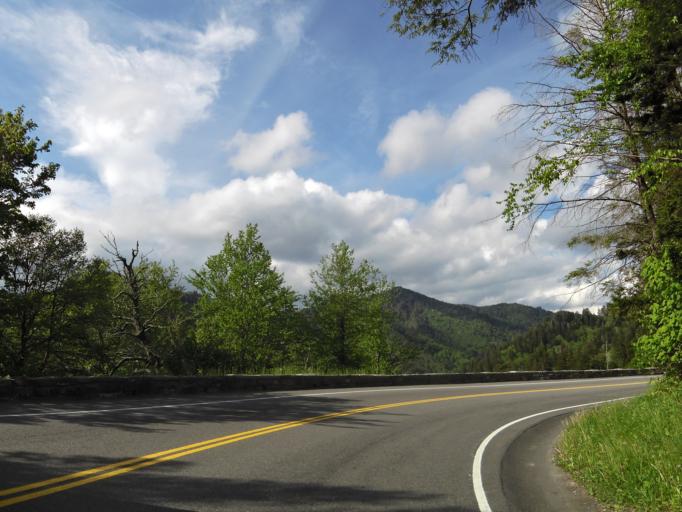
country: US
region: Tennessee
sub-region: Sevier County
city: Gatlinburg
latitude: 35.6156
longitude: -83.4255
